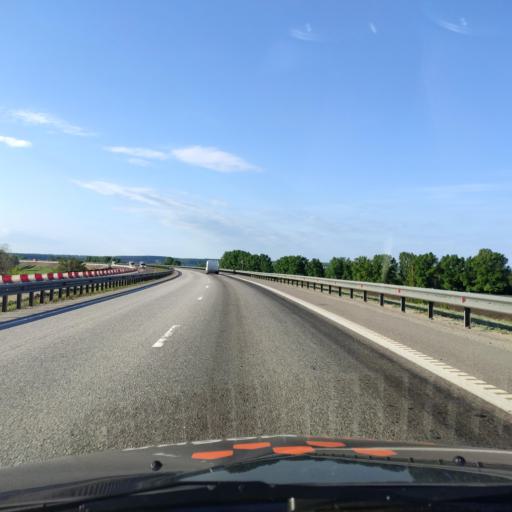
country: RU
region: Lipetsk
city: Khlevnoye
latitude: 52.0676
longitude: 39.1798
